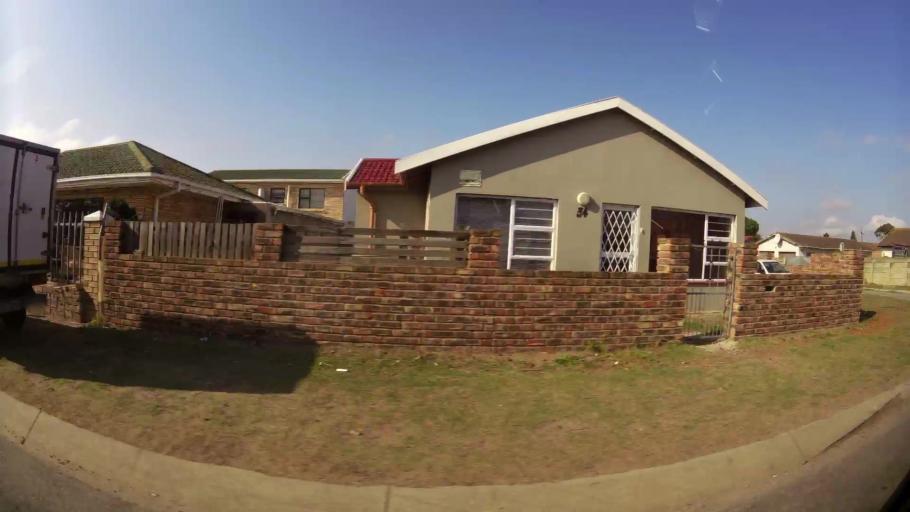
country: ZA
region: Eastern Cape
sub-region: Nelson Mandela Bay Metropolitan Municipality
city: Port Elizabeth
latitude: -33.9223
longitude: 25.5253
